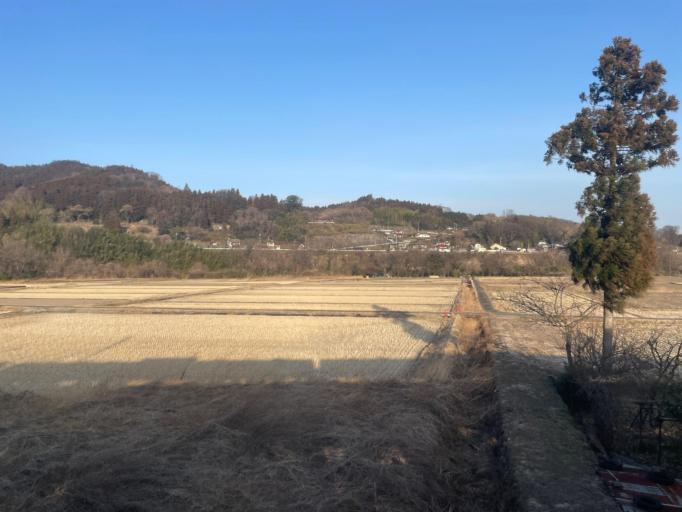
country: JP
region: Gunma
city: Shibukawa
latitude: 36.5430
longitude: 138.9566
